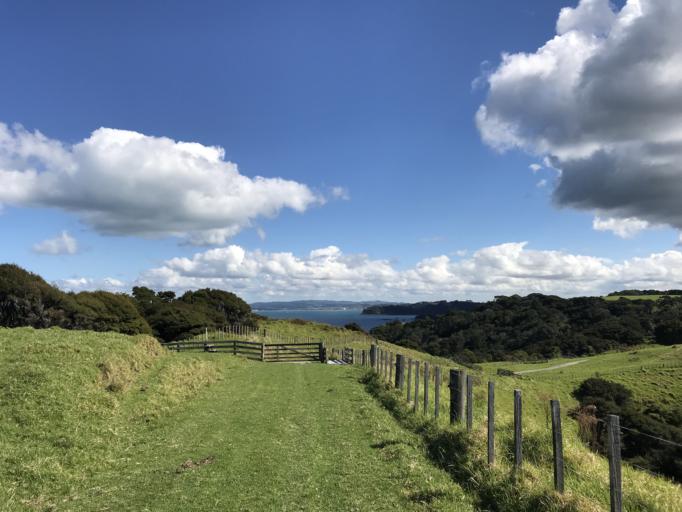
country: NZ
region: Auckland
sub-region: Auckland
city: Warkworth
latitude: -36.3761
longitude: 174.8343
